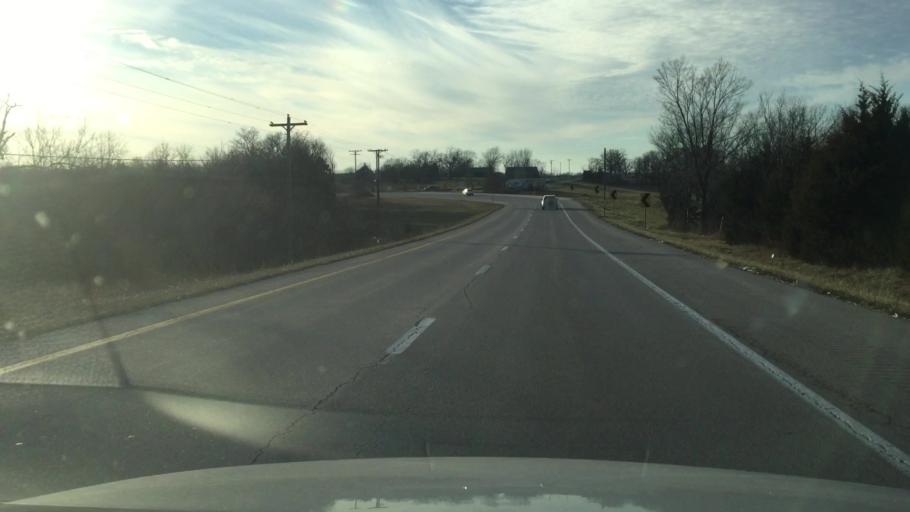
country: US
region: Missouri
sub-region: Cole County
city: Wardsville
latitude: 38.4321
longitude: -92.3187
